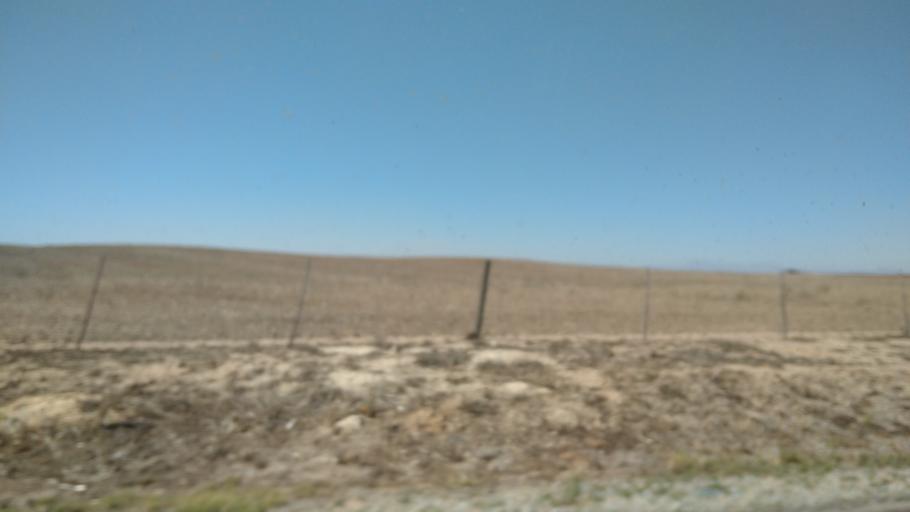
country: ZA
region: Western Cape
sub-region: West Coast District Municipality
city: Moorreesburg
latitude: -33.1954
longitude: 18.5100
